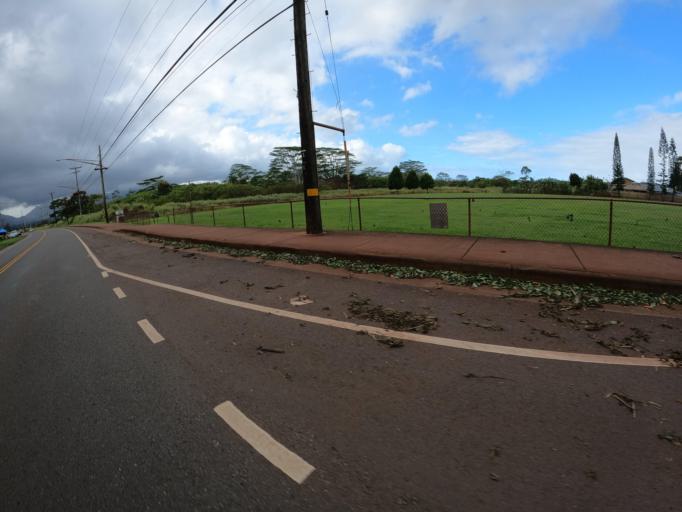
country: US
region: Hawaii
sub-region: Honolulu County
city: Whitmore Village
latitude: 21.5094
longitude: -158.0270
